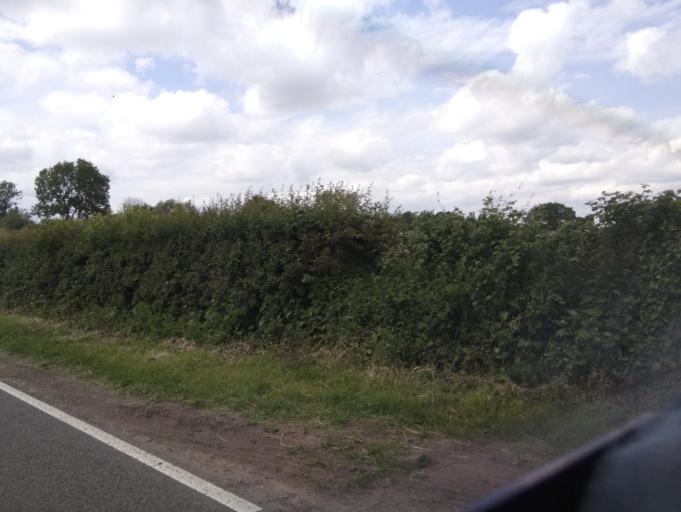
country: GB
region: England
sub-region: Herefordshire
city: Sellack
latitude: 51.9165
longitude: -2.6293
